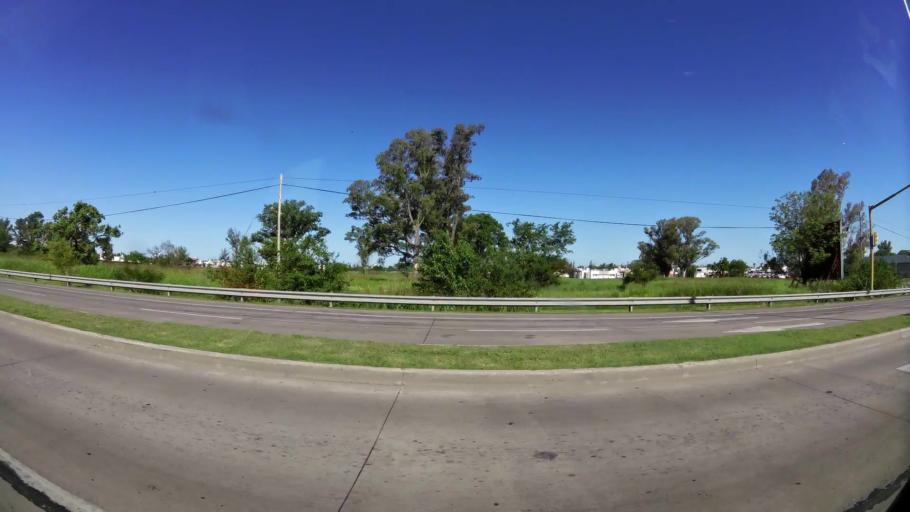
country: AR
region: Santa Fe
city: Rafaela
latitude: -31.2650
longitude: -61.5083
